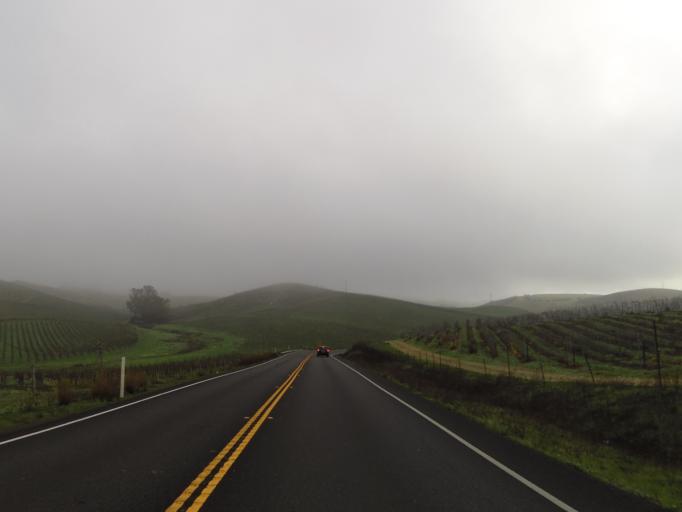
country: US
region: California
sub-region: Sonoma County
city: Sonoma
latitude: 38.2524
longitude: -122.4048
